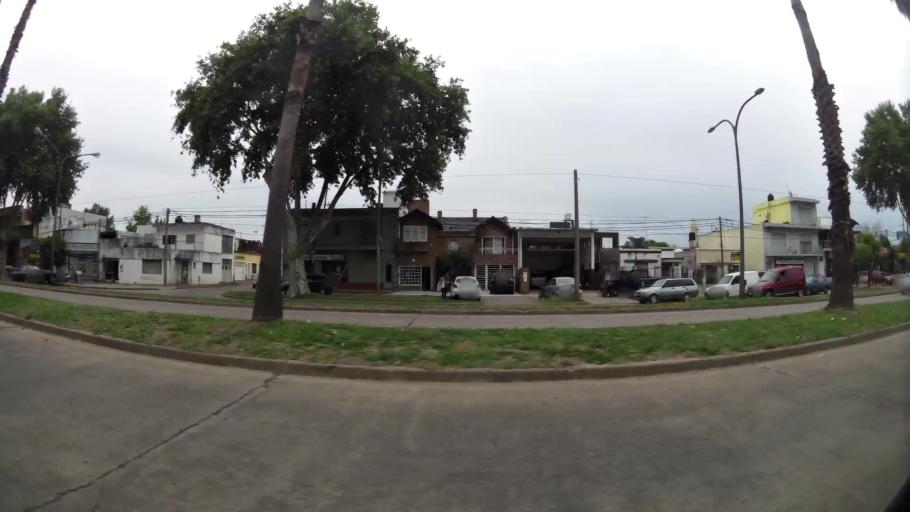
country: AR
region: Santa Fe
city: Granadero Baigorria
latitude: -32.8752
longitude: -60.6982
